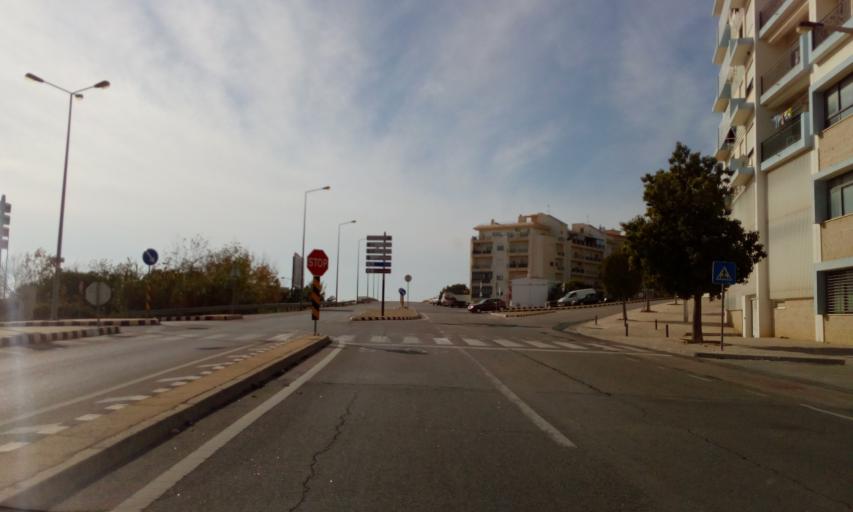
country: PT
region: Faro
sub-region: Faro
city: Faro
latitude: 37.0163
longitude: -7.9155
